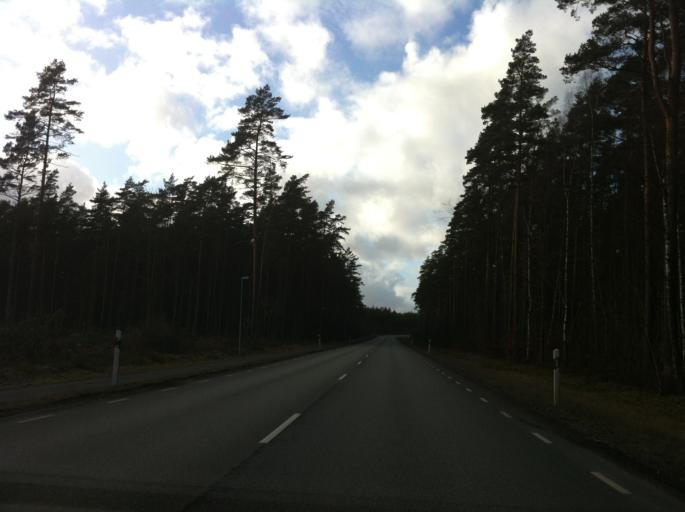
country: SE
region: Skane
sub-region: Bromolla Kommun
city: Bromoella
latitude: 56.0625
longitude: 14.5048
